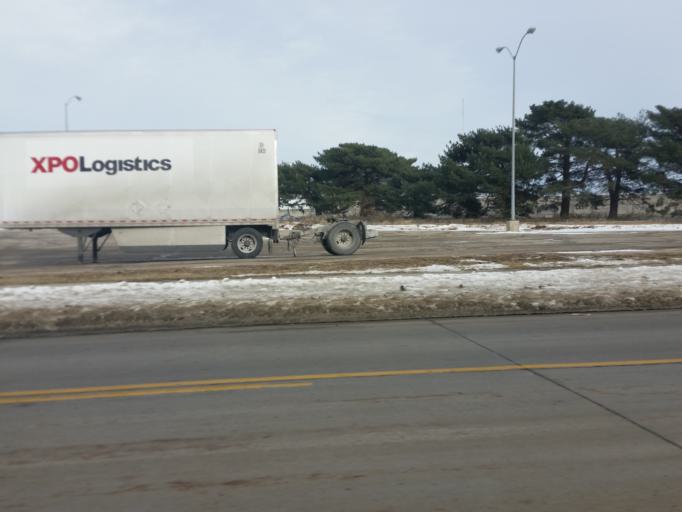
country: US
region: Iowa
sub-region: Black Hawk County
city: Waterloo
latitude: 42.4998
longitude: -92.3468
